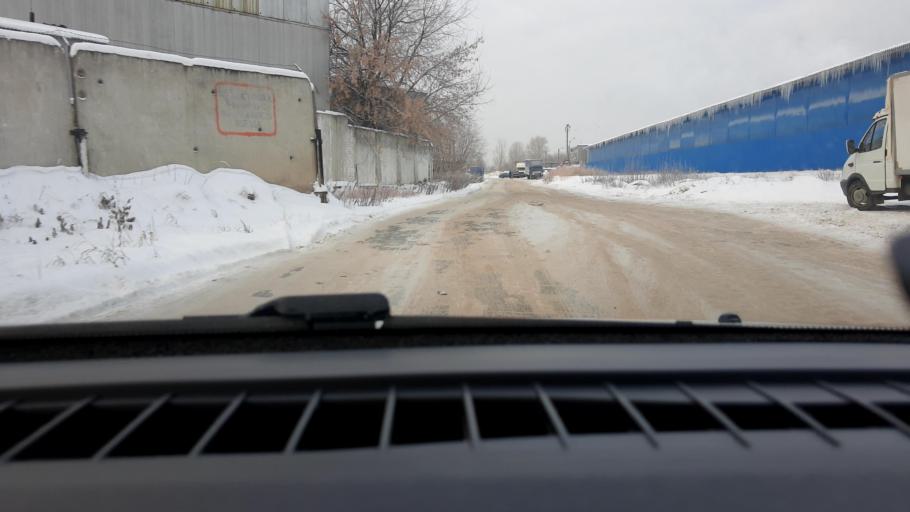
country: RU
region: Nizjnij Novgorod
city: Gorbatovka
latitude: 56.3384
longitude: 43.8184
